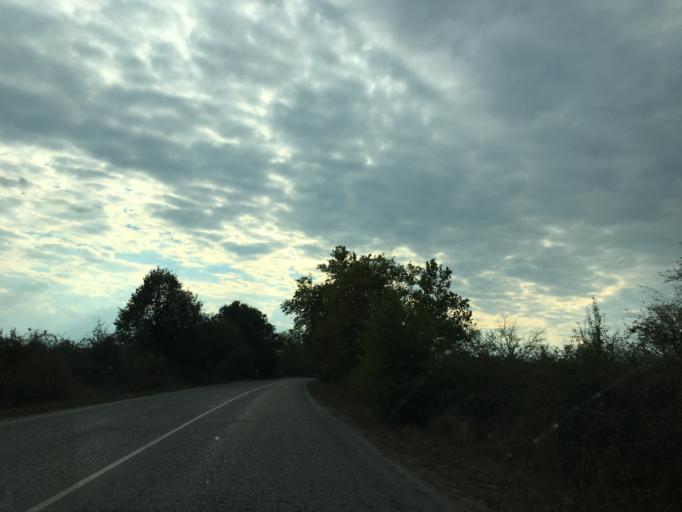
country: BG
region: Vratsa
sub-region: Obshtina Vratsa
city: Vratsa
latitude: 43.2902
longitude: 23.6503
